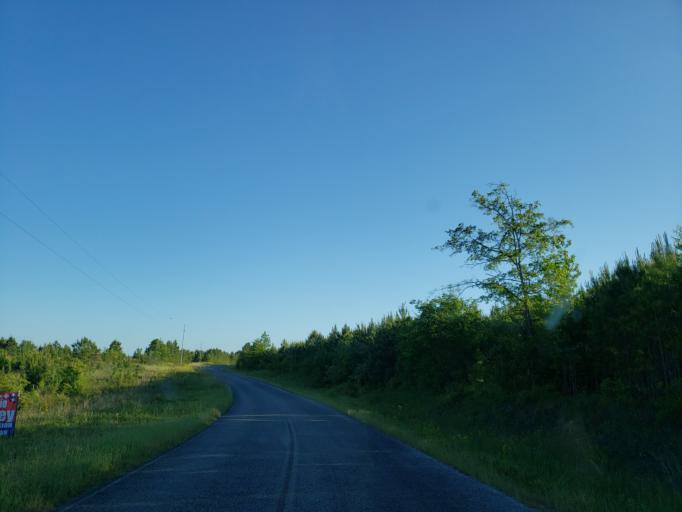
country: US
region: Georgia
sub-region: Haralson County
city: Tallapoosa
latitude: 33.7810
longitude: -85.3237
